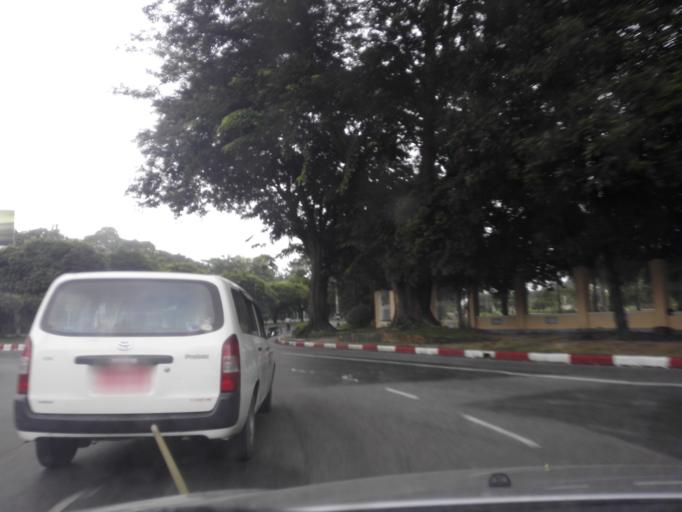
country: MM
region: Yangon
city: Yangon
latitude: 16.7950
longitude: 96.1471
